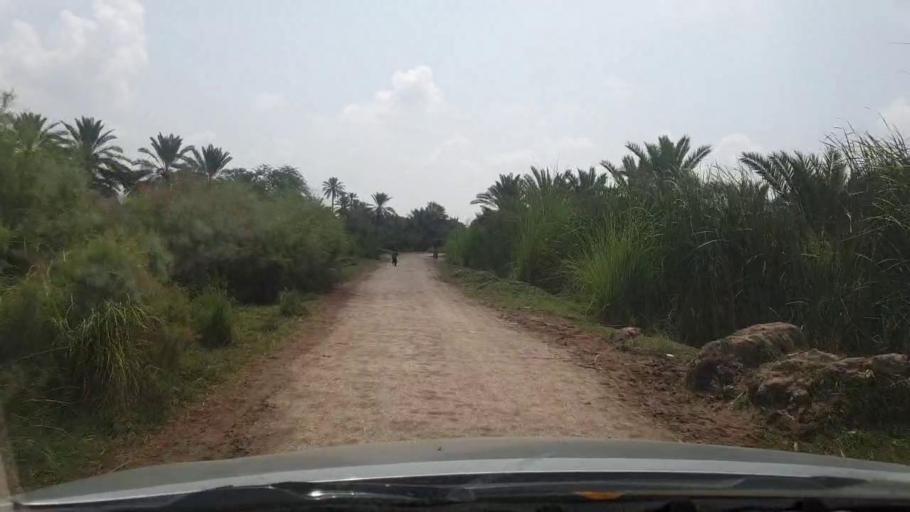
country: PK
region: Sindh
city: Khairpur
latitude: 27.4860
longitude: 68.7279
